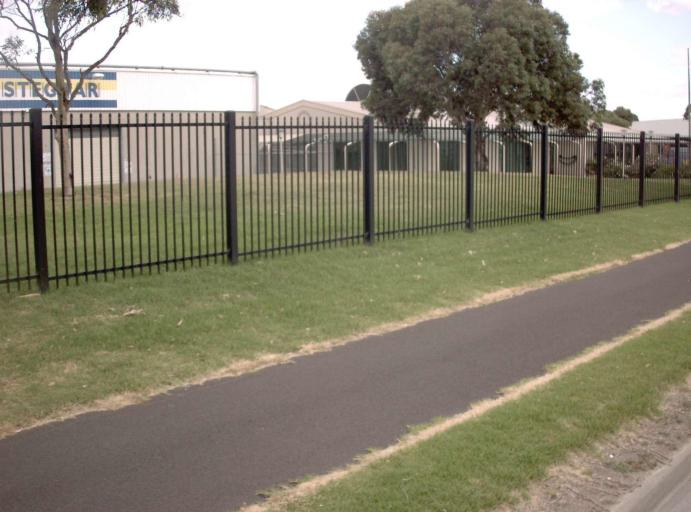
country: AU
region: Victoria
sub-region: Knox
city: Scoresby
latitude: -37.9076
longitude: 145.2372
